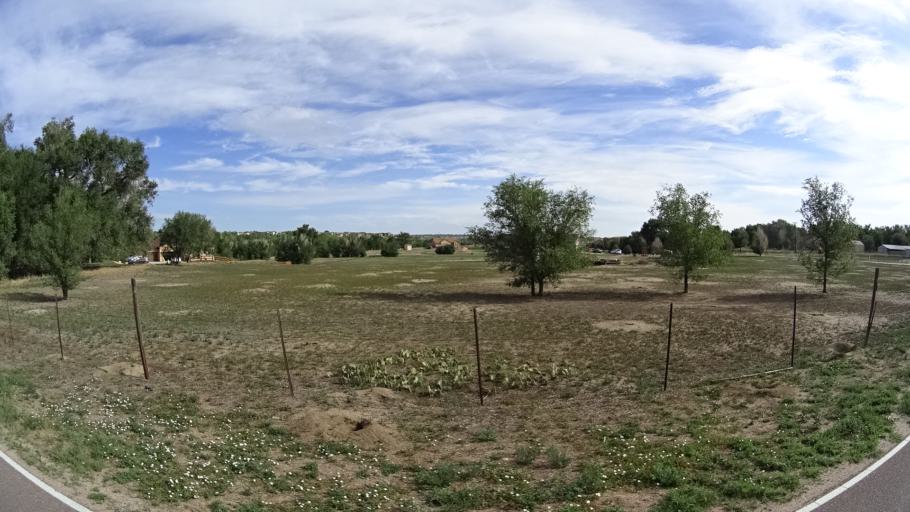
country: US
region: Colorado
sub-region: El Paso County
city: Fountain
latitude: 38.6841
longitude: -104.6858
